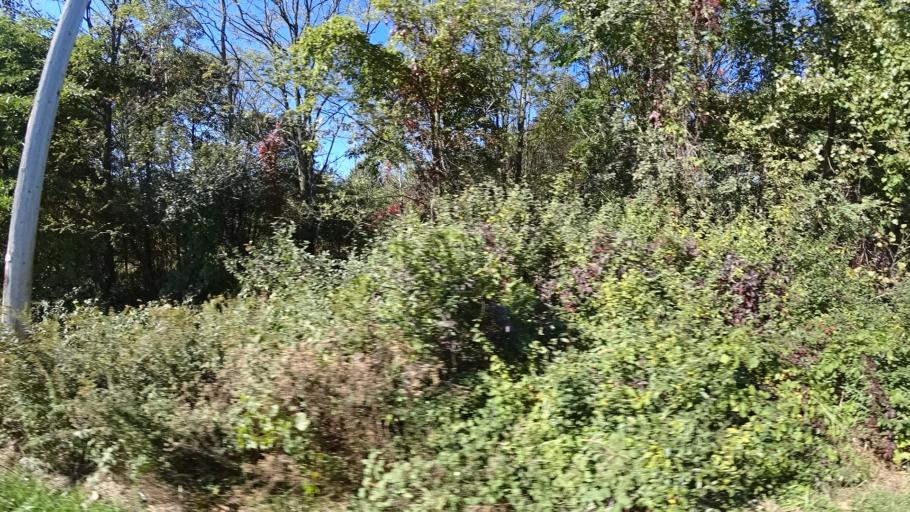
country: US
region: Indiana
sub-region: LaPorte County
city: Michigan City
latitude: 41.7032
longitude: -86.9218
